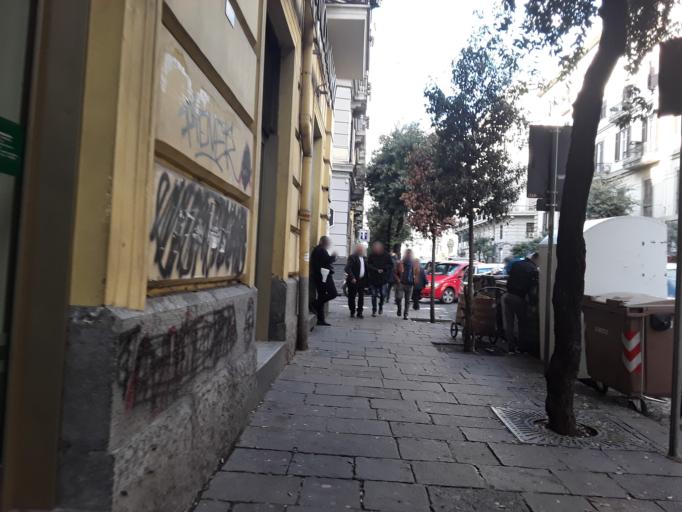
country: IT
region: Campania
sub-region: Provincia di Napoli
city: Napoli
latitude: 40.8610
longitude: 14.2665
